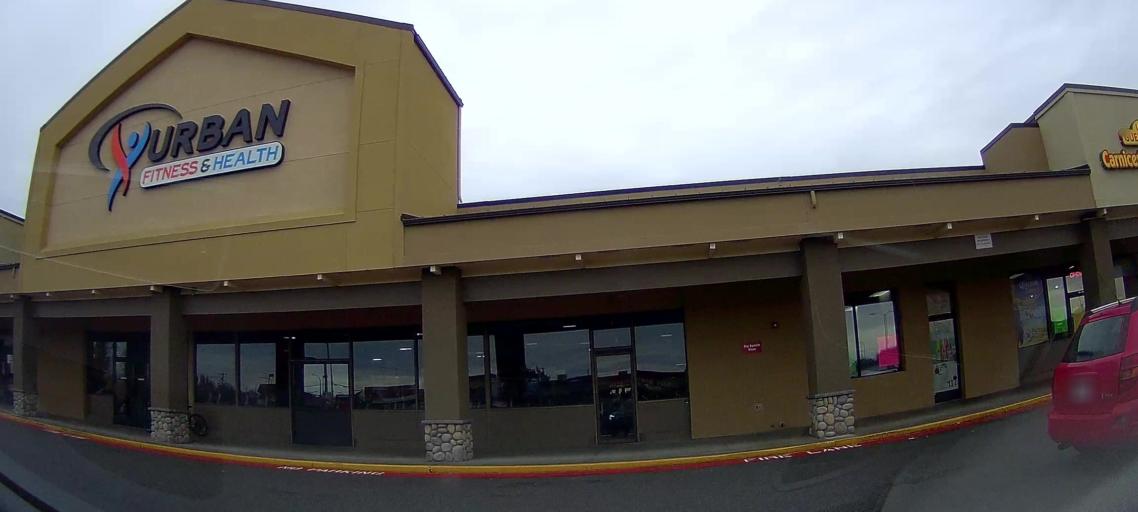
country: US
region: Washington
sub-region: Skagit County
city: Mount Vernon
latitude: 48.4368
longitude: -122.3333
